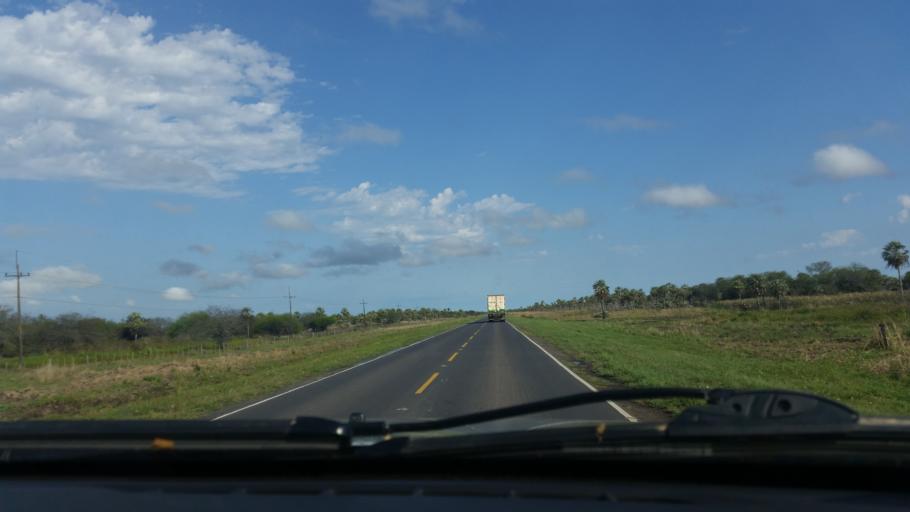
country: PY
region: Presidente Hayes
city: Benjamin Aceval
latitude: -24.9190
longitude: -57.6050
